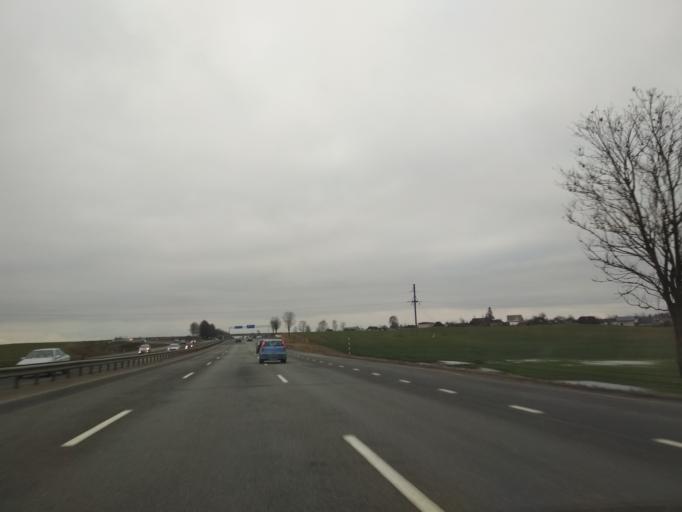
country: BY
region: Minsk
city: Pryvol'ny
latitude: 53.7966
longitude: 27.8106
